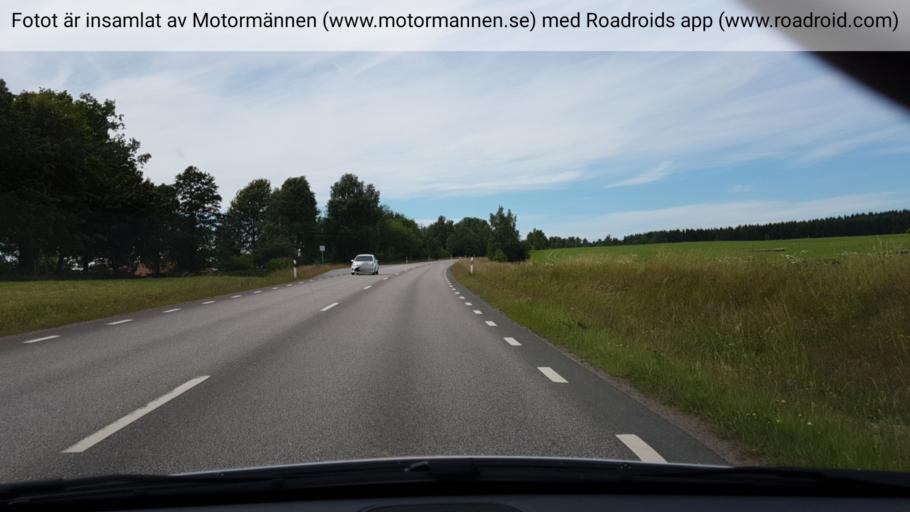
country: SE
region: Vaestra Goetaland
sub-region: Hjo Kommun
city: Hjo
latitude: 58.3236
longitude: 14.2629
